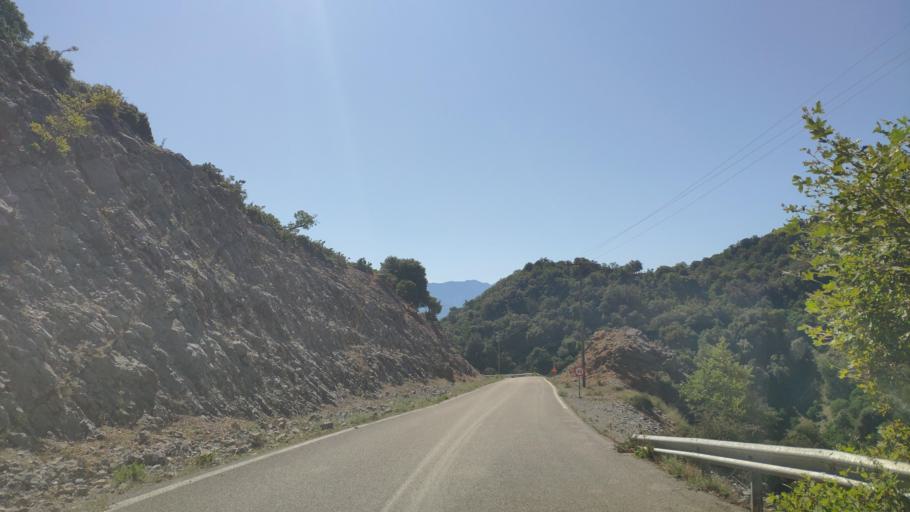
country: GR
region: Central Greece
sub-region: Nomos Evrytanias
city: Kerasochori
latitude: 38.9673
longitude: 21.4680
